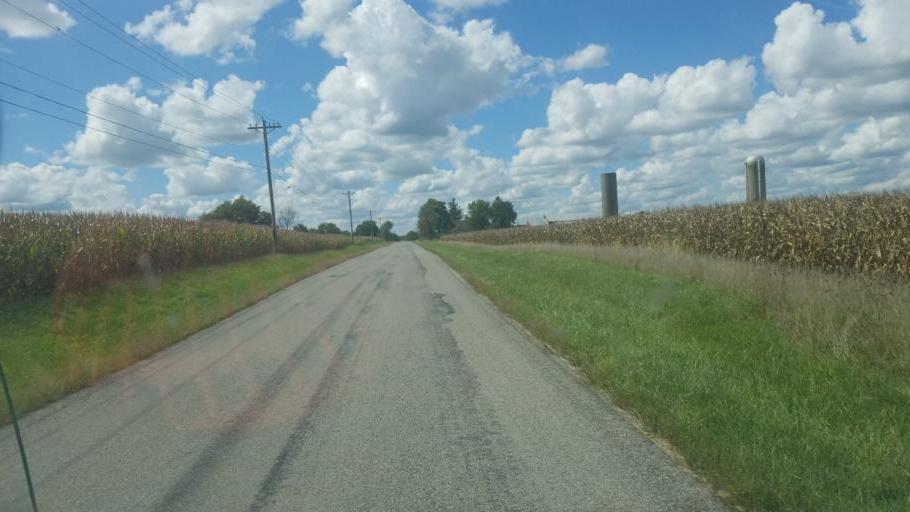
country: US
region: Ohio
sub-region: Champaign County
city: North Lewisburg
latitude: 40.3275
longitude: -83.4825
